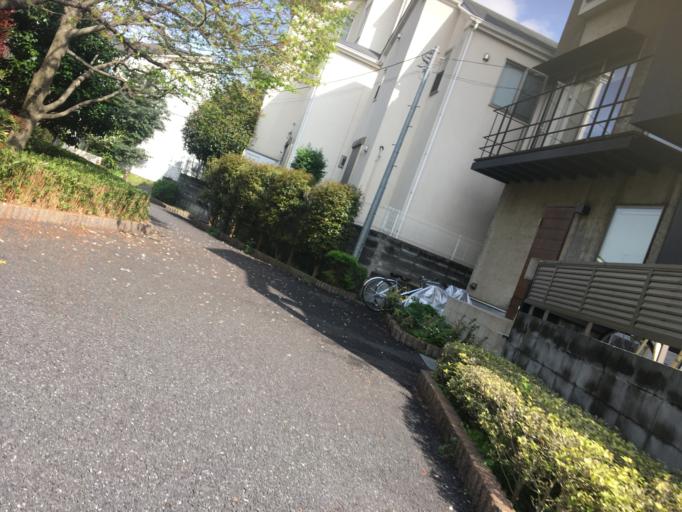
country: JP
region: Tokyo
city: Tokyo
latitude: 35.7198
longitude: 139.6319
